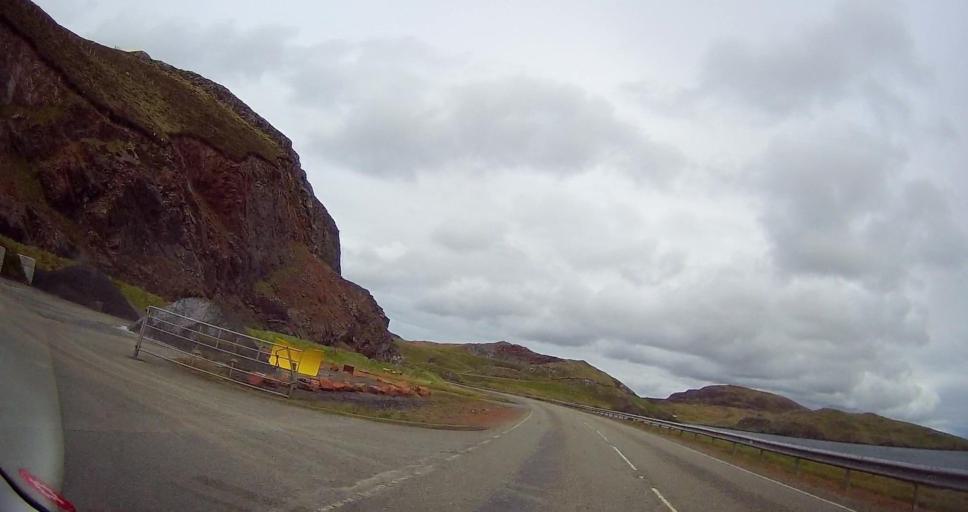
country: GB
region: Scotland
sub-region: Shetland Islands
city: Lerwick
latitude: 60.3944
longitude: -1.3783
